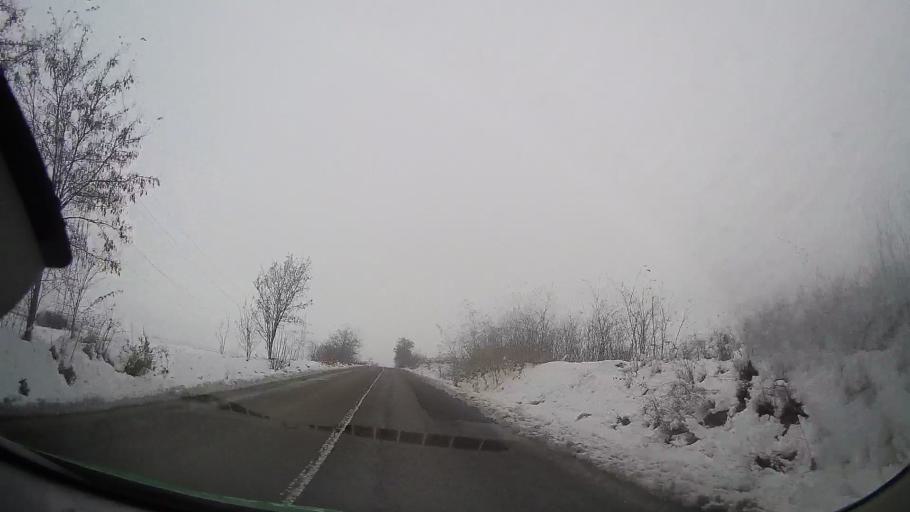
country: RO
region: Vaslui
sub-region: Comuna Vulturesti
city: Vulturesti
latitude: 46.7802
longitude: 27.5762
